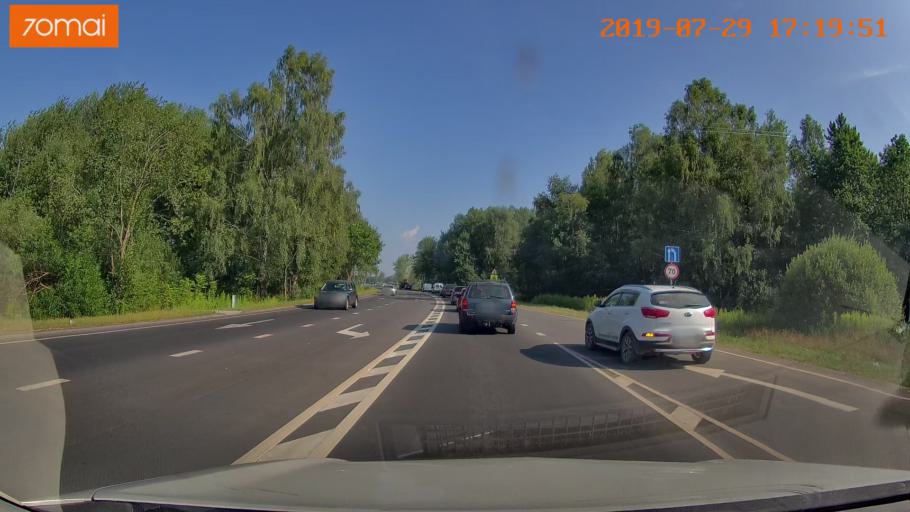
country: RU
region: Kaliningrad
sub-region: Gorod Kaliningrad
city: Kaliningrad
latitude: 54.7703
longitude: 20.4248
